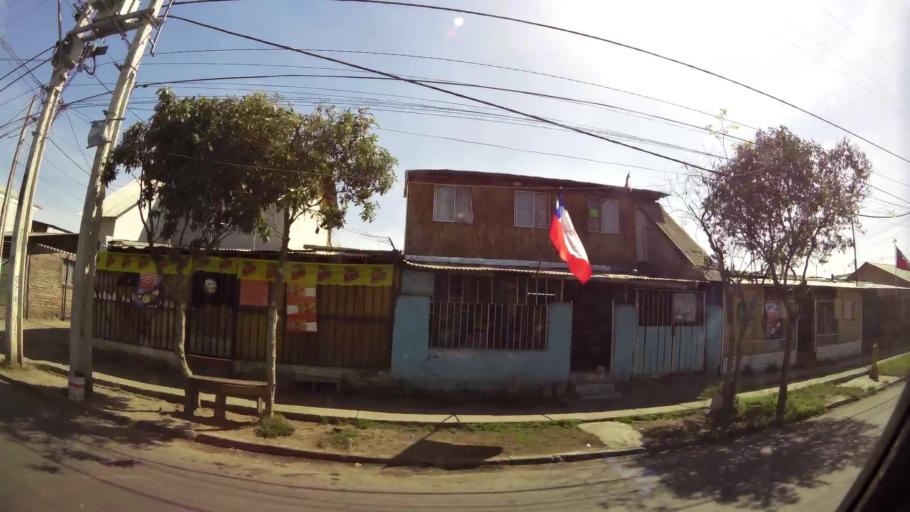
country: CL
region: Santiago Metropolitan
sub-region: Provincia de Maipo
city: San Bernardo
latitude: -33.5259
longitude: -70.7037
